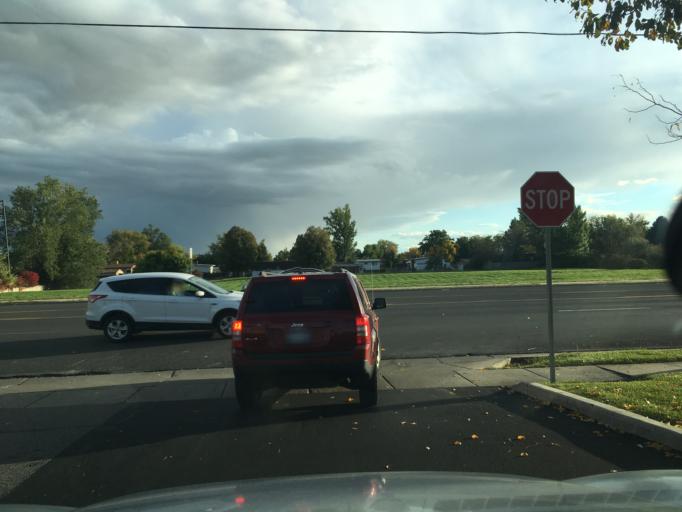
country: US
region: Utah
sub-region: Davis County
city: Layton
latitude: 41.0748
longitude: -111.9513
